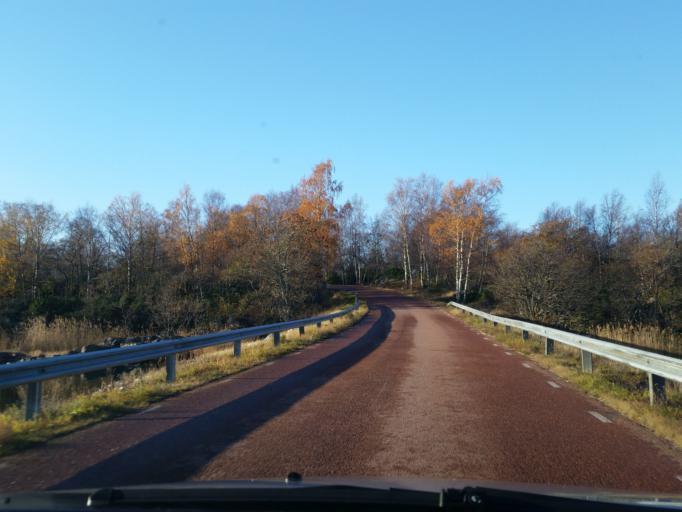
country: AX
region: Alands skaergard
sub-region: Braendoe
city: Braendoe
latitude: 60.4264
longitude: 21.0000
